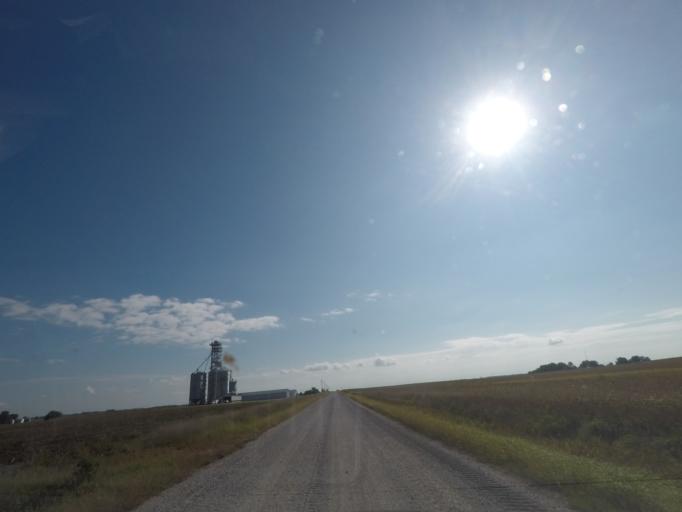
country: US
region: Iowa
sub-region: Story County
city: Nevada
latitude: 42.0489
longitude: -93.4133
